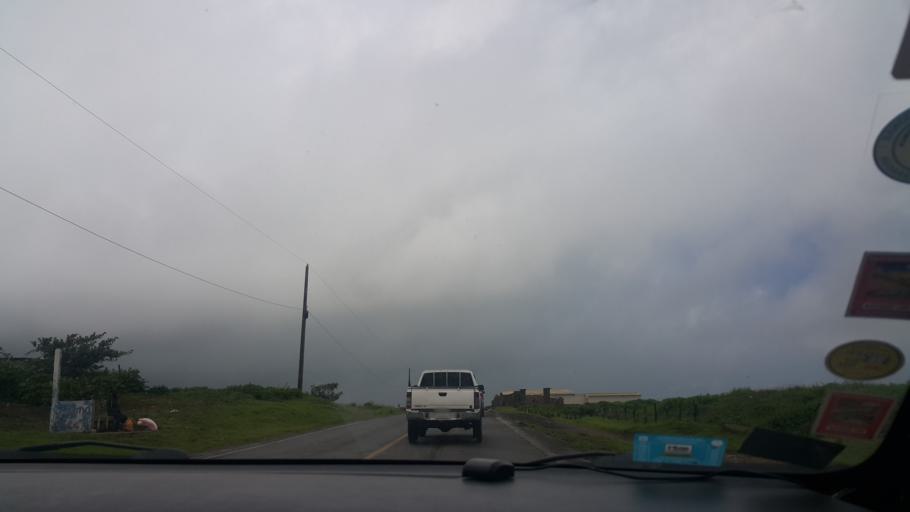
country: NI
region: Managua
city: El Crucero
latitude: 11.9450
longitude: -86.2989
